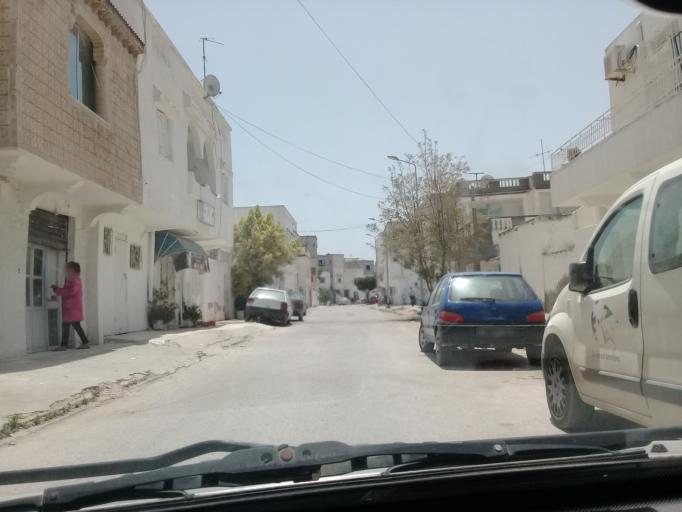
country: TN
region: Ariana
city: Ariana
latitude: 36.8332
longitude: 10.1981
